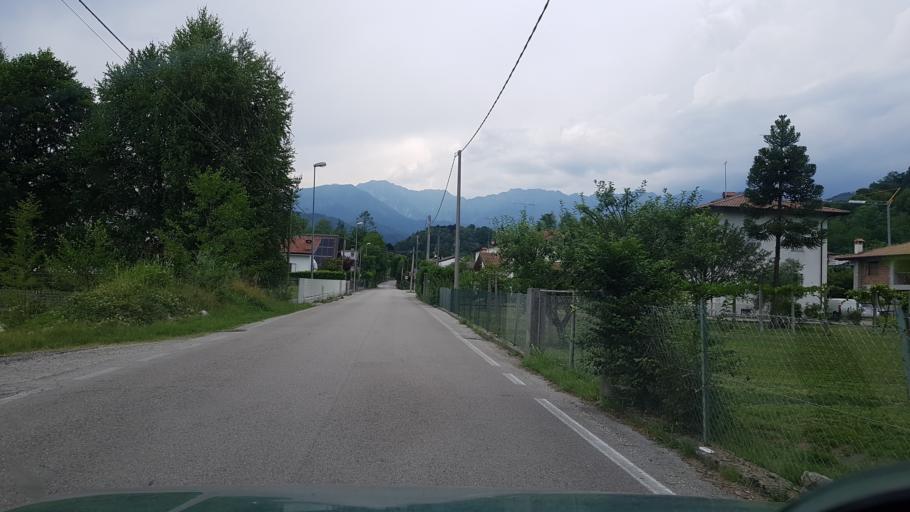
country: IT
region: Friuli Venezia Giulia
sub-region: Provincia di Udine
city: Tarcento
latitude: 46.2115
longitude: 13.2282
